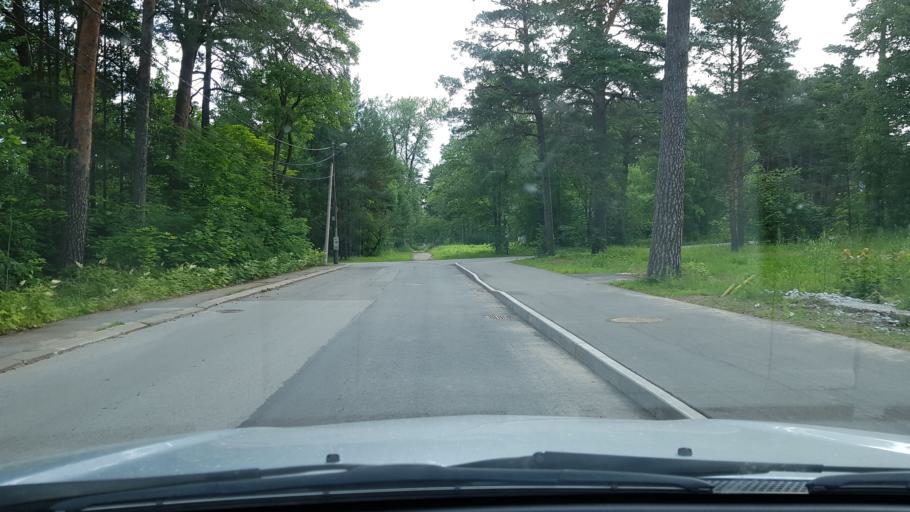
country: EE
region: Ida-Virumaa
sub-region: Narva-Joesuu linn
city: Narva-Joesuu
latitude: 59.4558
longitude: 28.0381
